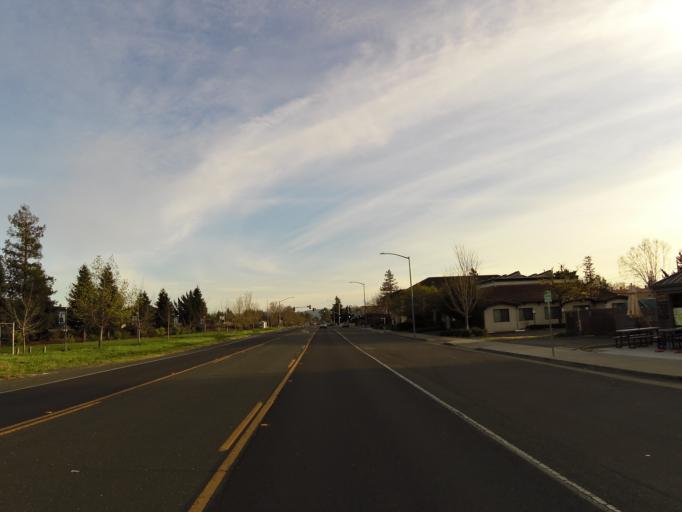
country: US
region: California
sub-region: Sonoma County
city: Sonoma
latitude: 38.2829
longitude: -122.4594
